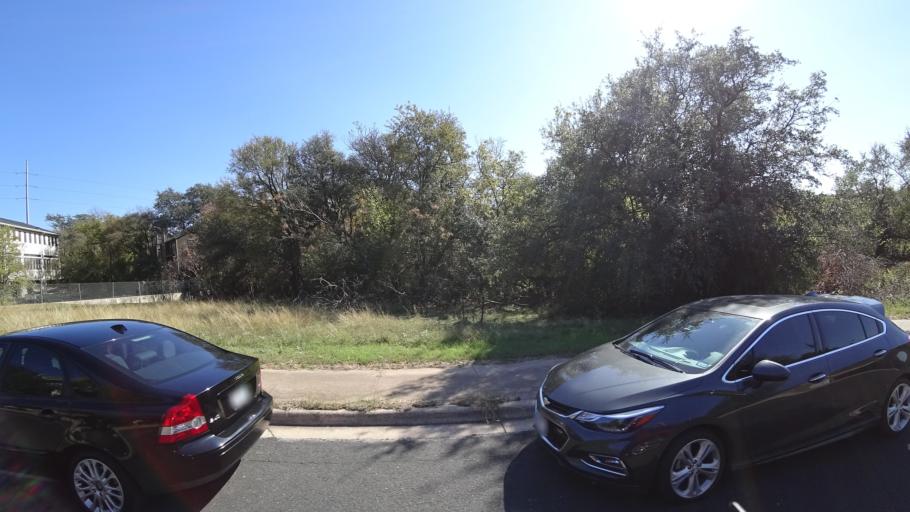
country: US
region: Texas
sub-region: Williamson County
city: Jollyville
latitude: 30.4097
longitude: -97.7490
